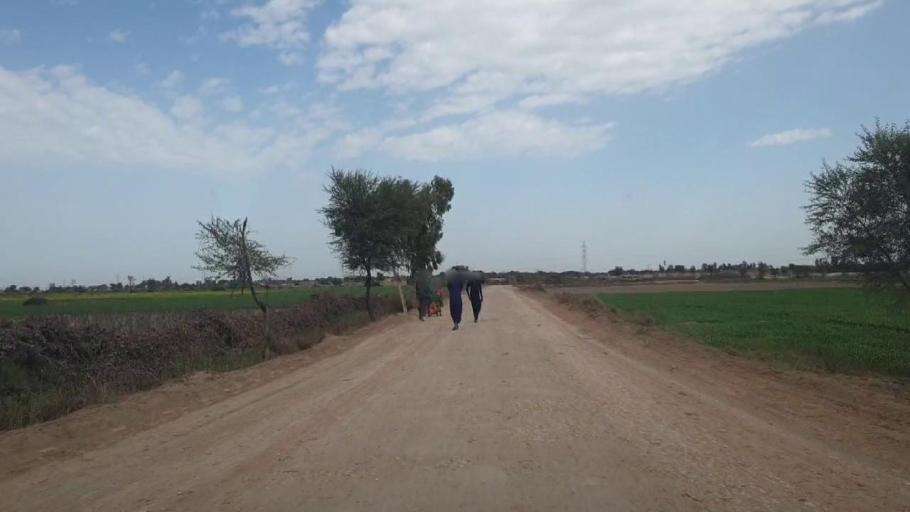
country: PK
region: Sindh
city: Sakrand
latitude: 26.0096
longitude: 68.3472
